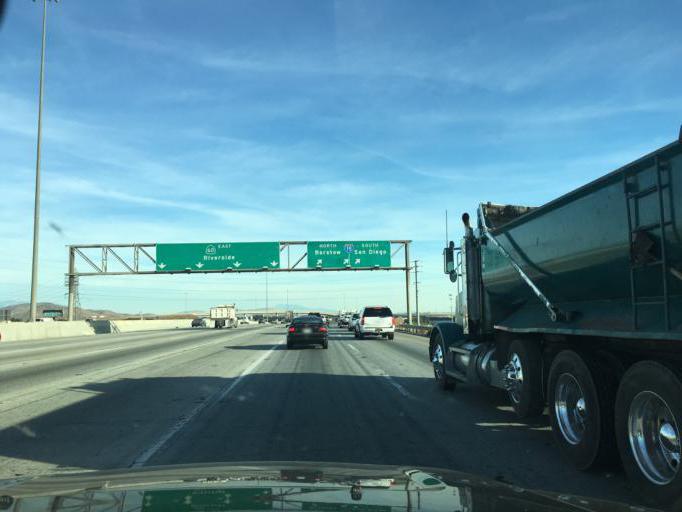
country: US
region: California
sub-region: Riverside County
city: Mira Loma
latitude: 34.0243
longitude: -117.5602
